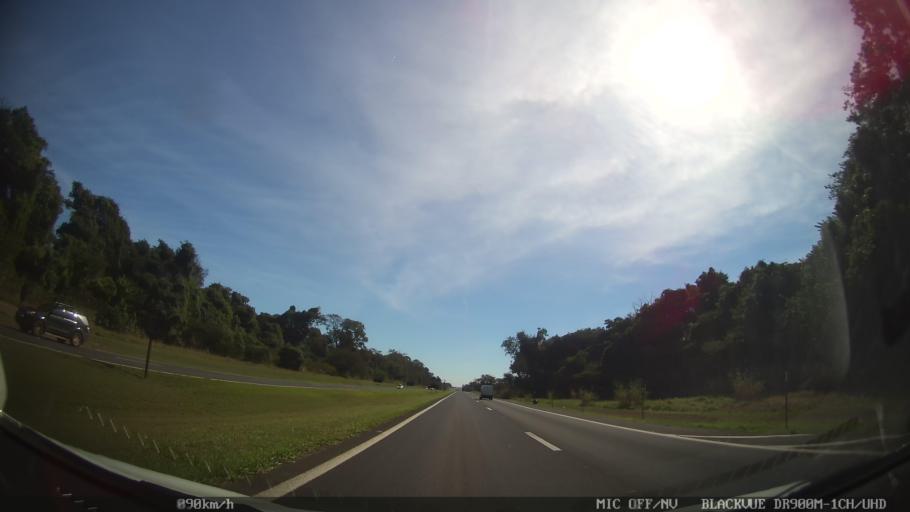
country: BR
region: Sao Paulo
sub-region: Pirassununga
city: Pirassununga
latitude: -21.9515
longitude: -47.4616
